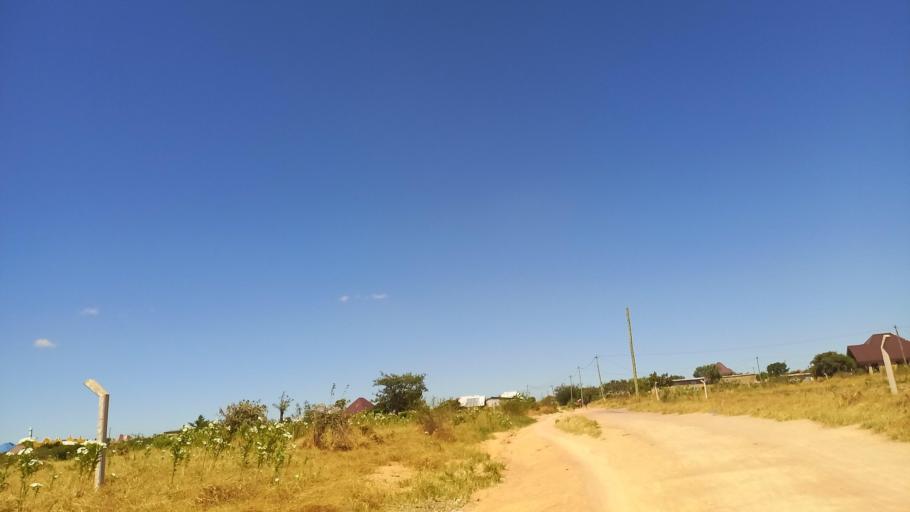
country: TZ
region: Dodoma
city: Dodoma
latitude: -6.1263
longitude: 35.6967
